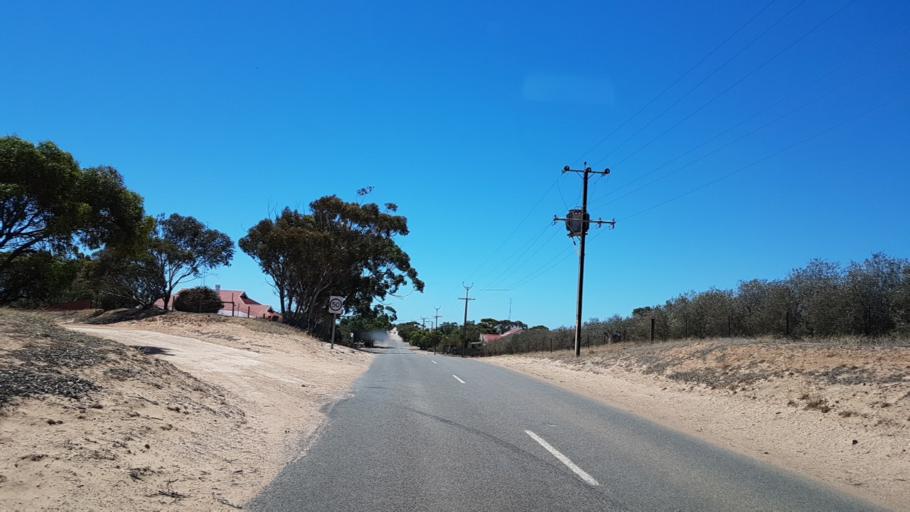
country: AU
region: South Australia
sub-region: Copper Coast
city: Wallaroo
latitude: -34.0480
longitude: 137.5930
